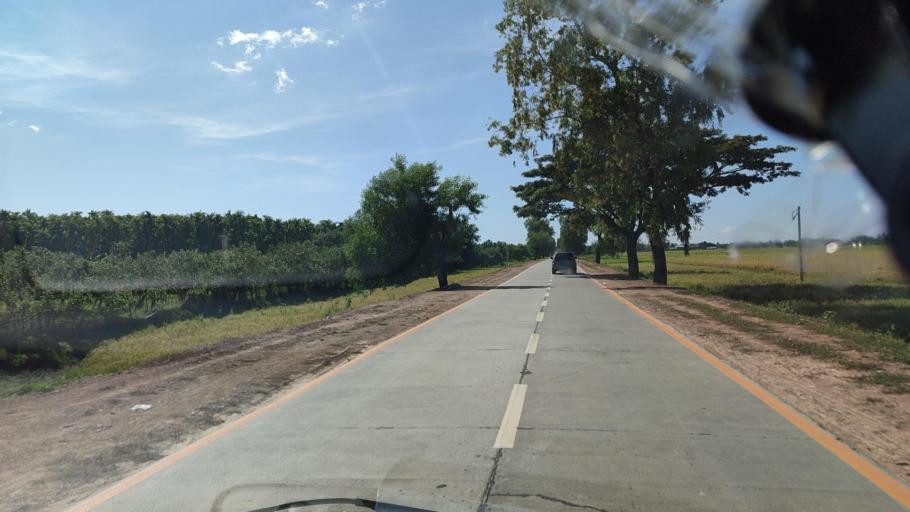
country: MM
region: Rakhine
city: Sittwe
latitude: 20.4788
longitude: 93.2787
